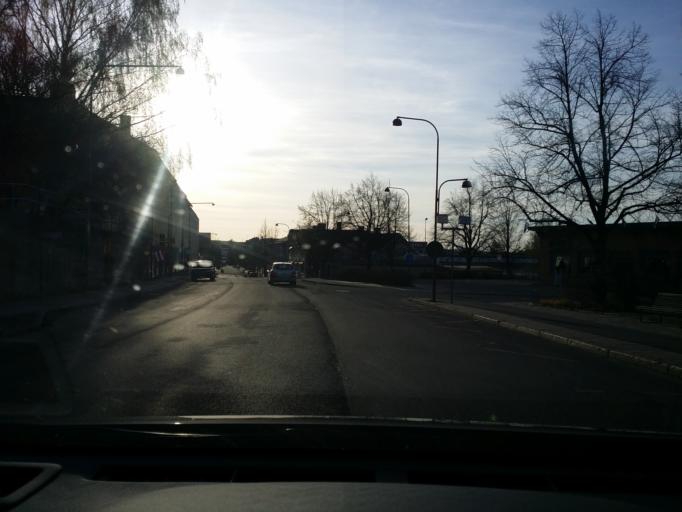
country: SE
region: Dalarna
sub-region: Avesta Kommun
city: Avesta
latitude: 60.1446
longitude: 16.1764
